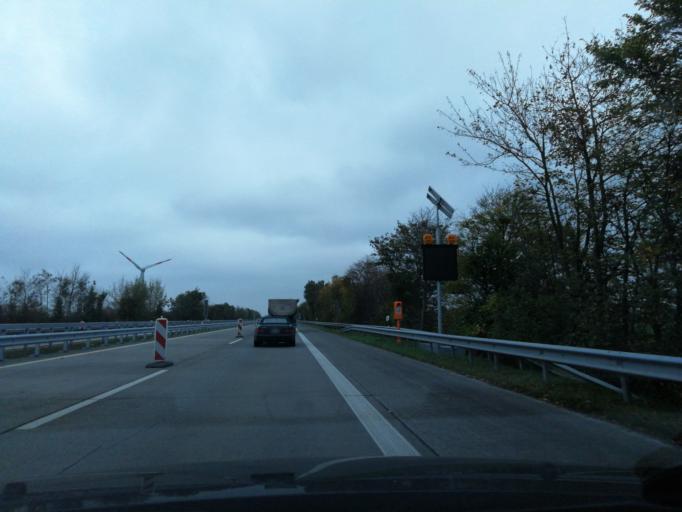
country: DE
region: Lower Saxony
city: Fedderwarden
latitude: 53.5409
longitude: 8.0363
